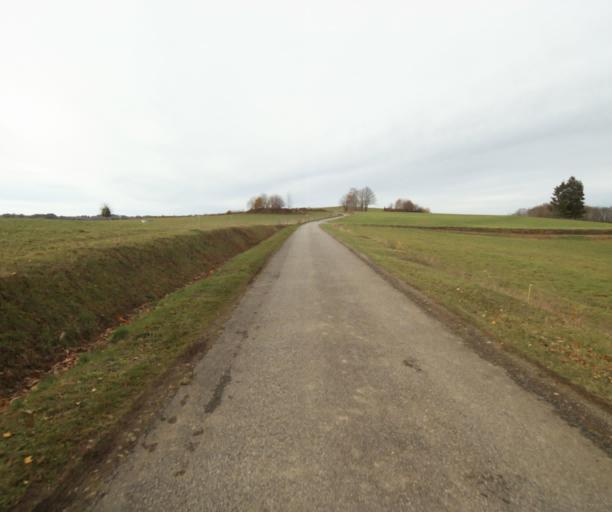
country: FR
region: Limousin
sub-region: Departement de la Correze
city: Sainte-Fortunade
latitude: 45.1617
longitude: 1.8103
